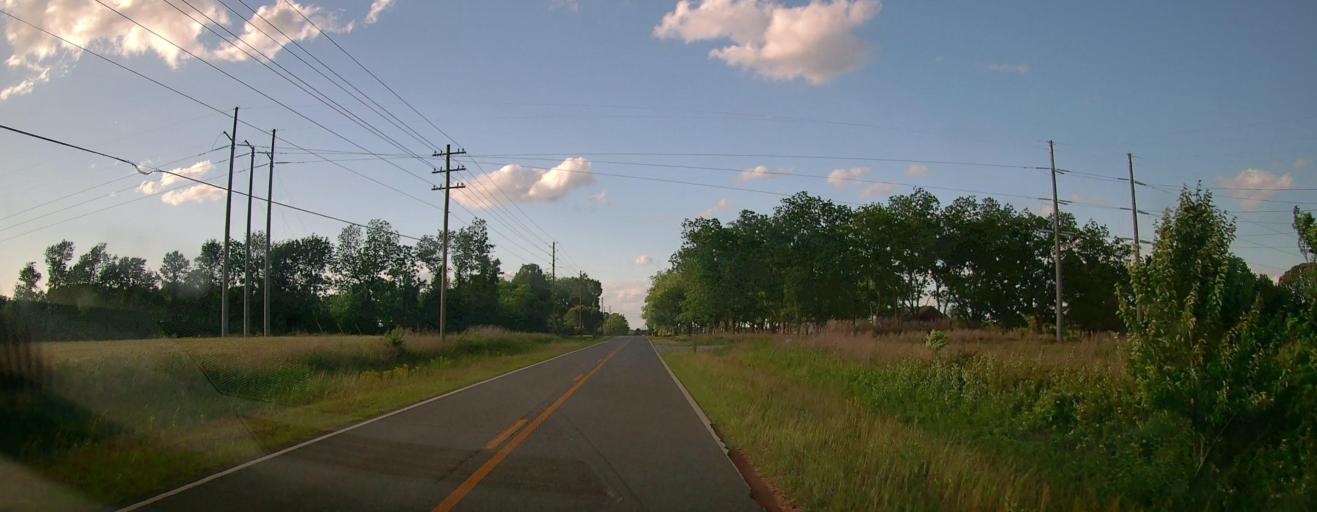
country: US
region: Georgia
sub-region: Peach County
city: Byron
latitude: 32.6258
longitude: -83.7673
